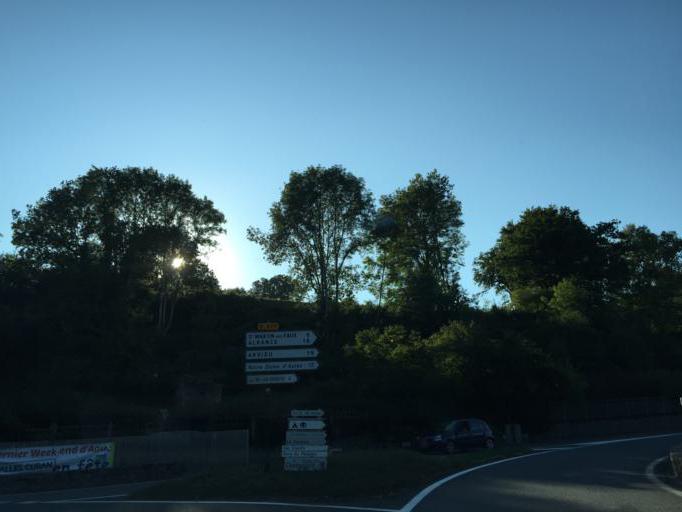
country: FR
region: Midi-Pyrenees
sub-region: Departement de l'Aveyron
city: Salles-Curan
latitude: 44.1882
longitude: 2.7889
